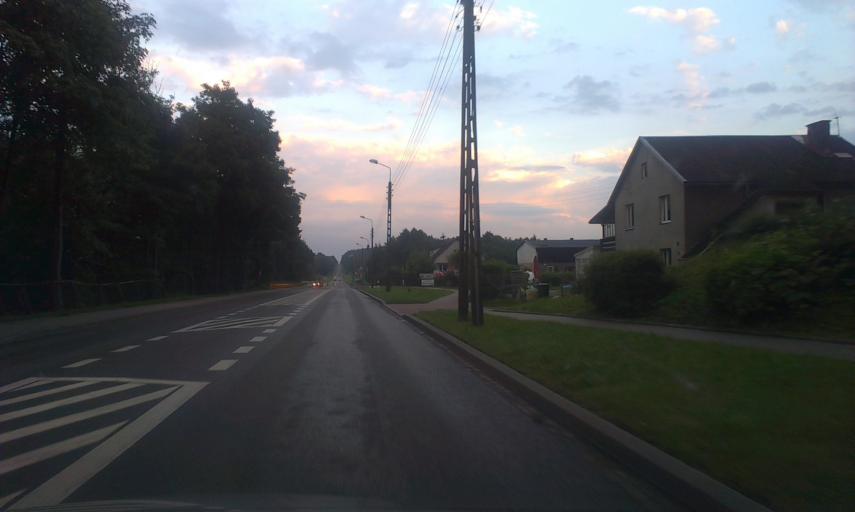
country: PL
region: West Pomeranian Voivodeship
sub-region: Powiat koszalinski
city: Sianow
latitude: 54.1248
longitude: 16.3027
